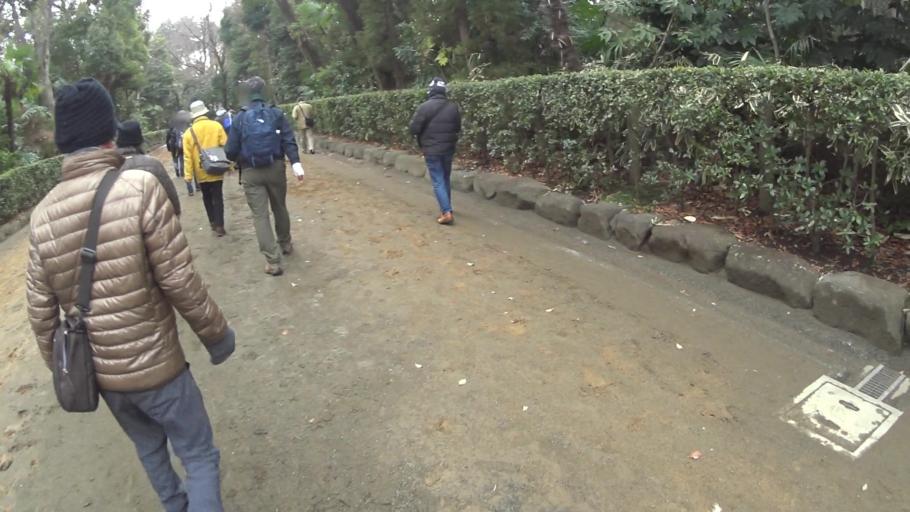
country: JP
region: Tokyo
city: Musashino
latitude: 35.7157
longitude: 139.5964
